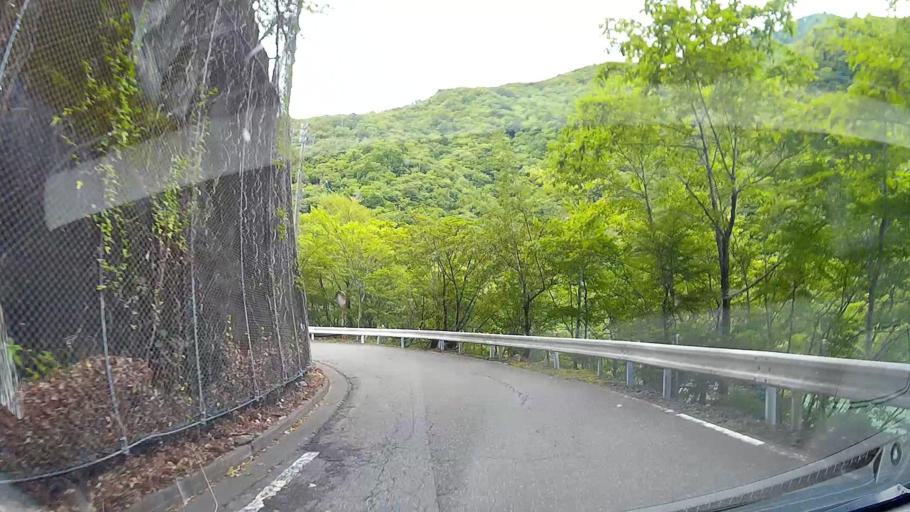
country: JP
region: Shizuoka
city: Shizuoka-shi
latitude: 35.3099
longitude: 138.1999
